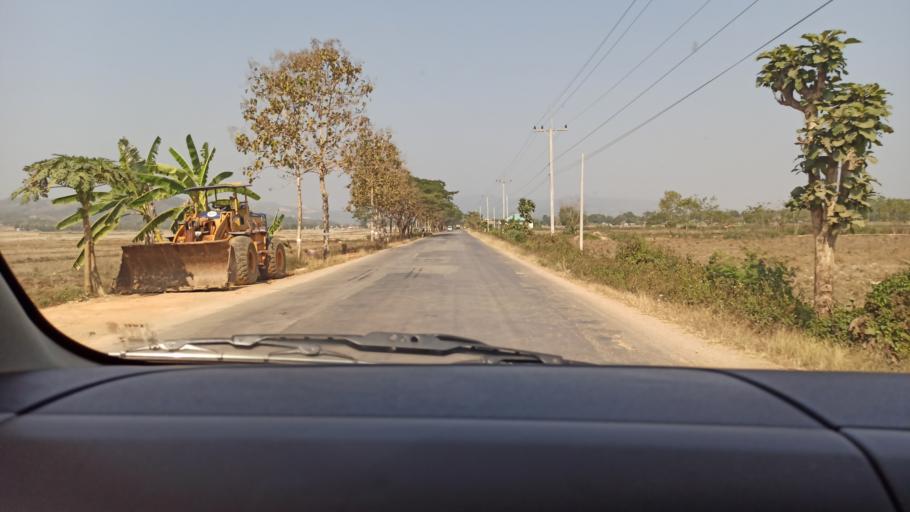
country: TH
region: Chiang Rai
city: Mae Sai
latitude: 20.5457
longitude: 99.9605
